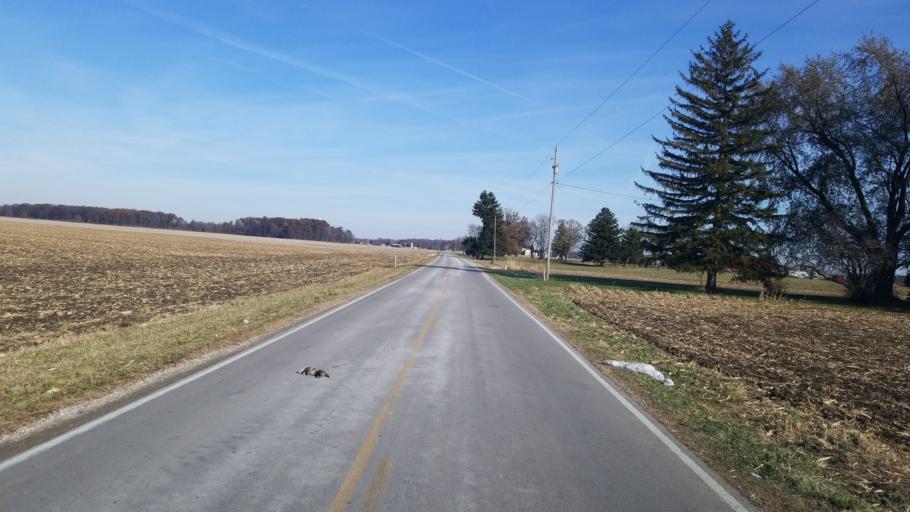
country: US
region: Ohio
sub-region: Huron County
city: Norwalk
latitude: 41.2049
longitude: -82.6563
